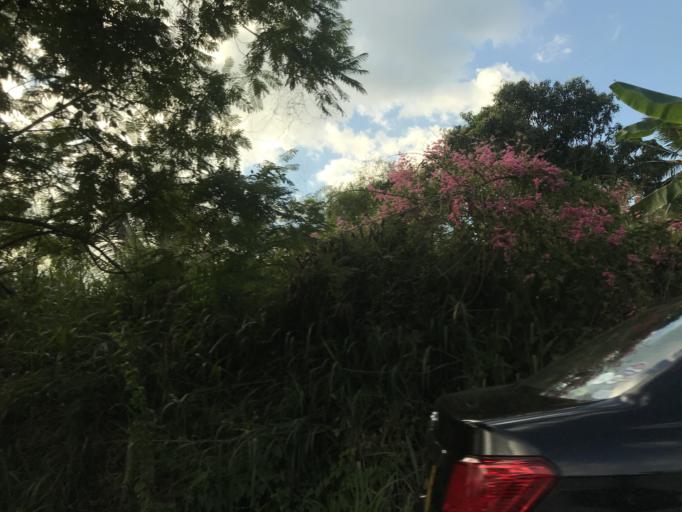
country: LK
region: Western
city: Gampaha
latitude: 7.0876
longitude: 79.9895
